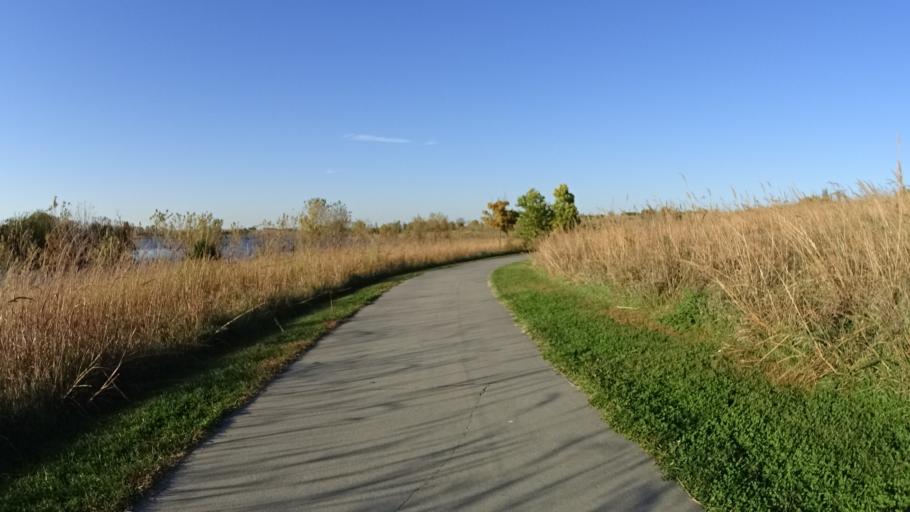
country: US
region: Nebraska
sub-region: Sarpy County
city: Papillion
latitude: 41.1353
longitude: -96.0657
